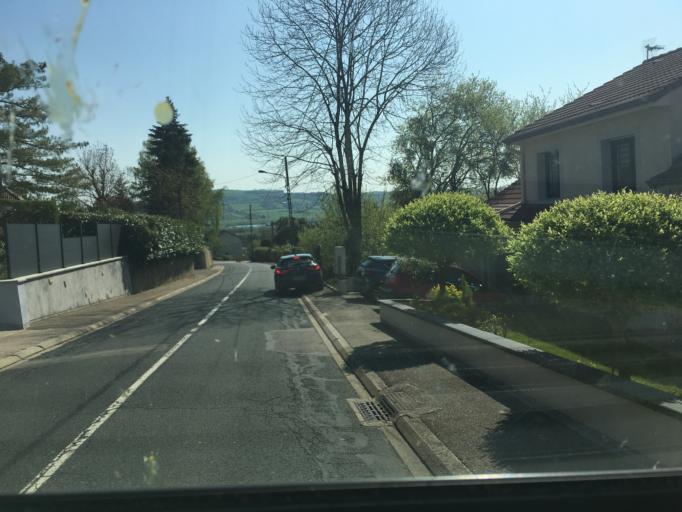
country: FR
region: Lorraine
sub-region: Departement de Meurthe-et-Moselle
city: Norroy-les-Pont-a-Mousson
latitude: 48.9342
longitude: 6.0317
